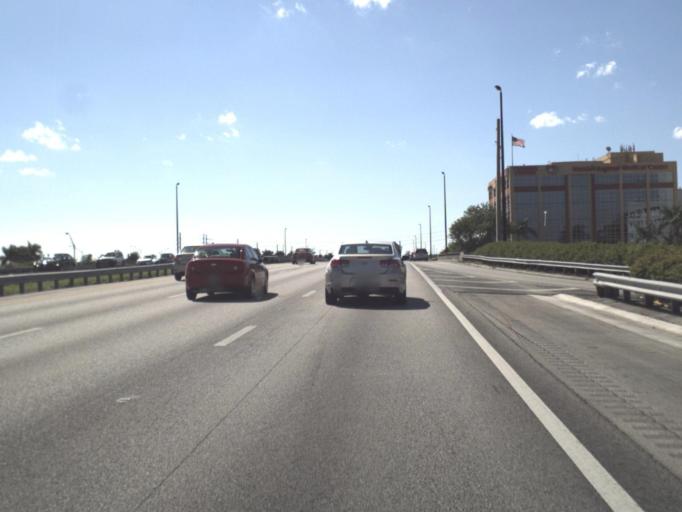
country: US
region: Florida
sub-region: Miami-Dade County
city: Westwood Lake
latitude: 25.7333
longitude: -80.3844
